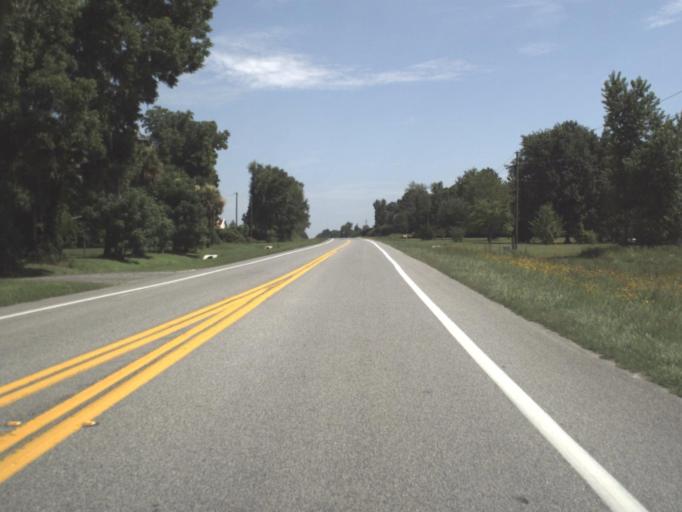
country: US
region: Florida
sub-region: Hamilton County
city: Jasper
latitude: 30.4099
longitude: -82.9338
